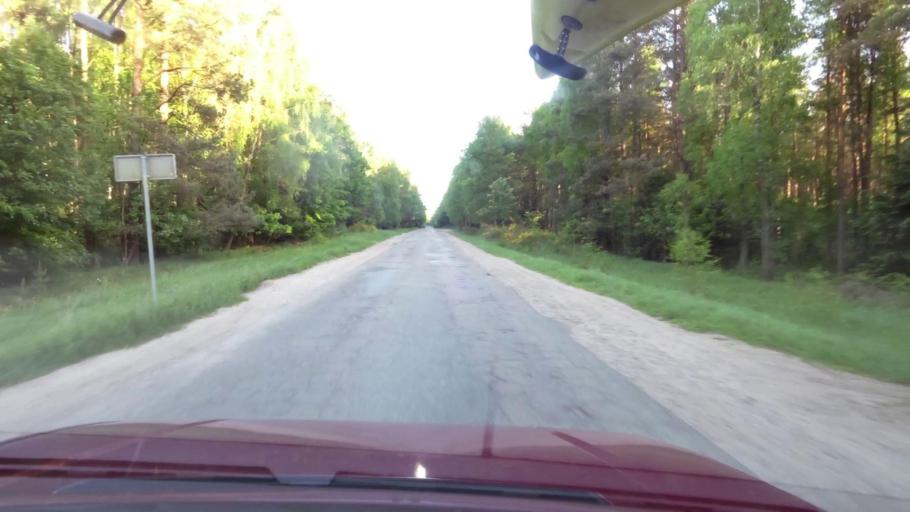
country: PL
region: West Pomeranian Voivodeship
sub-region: Powiat szczecinecki
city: Bialy Bor
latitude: 53.9326
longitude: 16.7986
